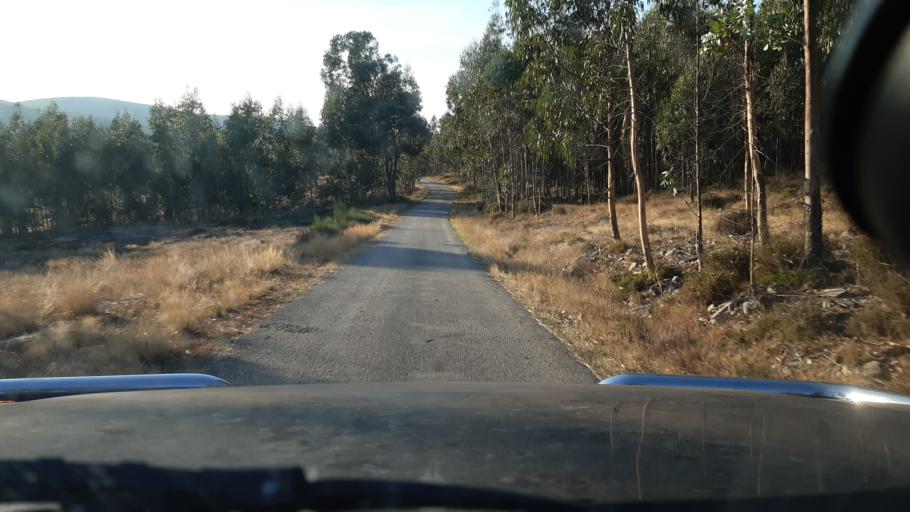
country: PT
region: Viseu
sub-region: Mortagua
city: Mortagua
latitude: 40.5456
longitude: -8.2592
